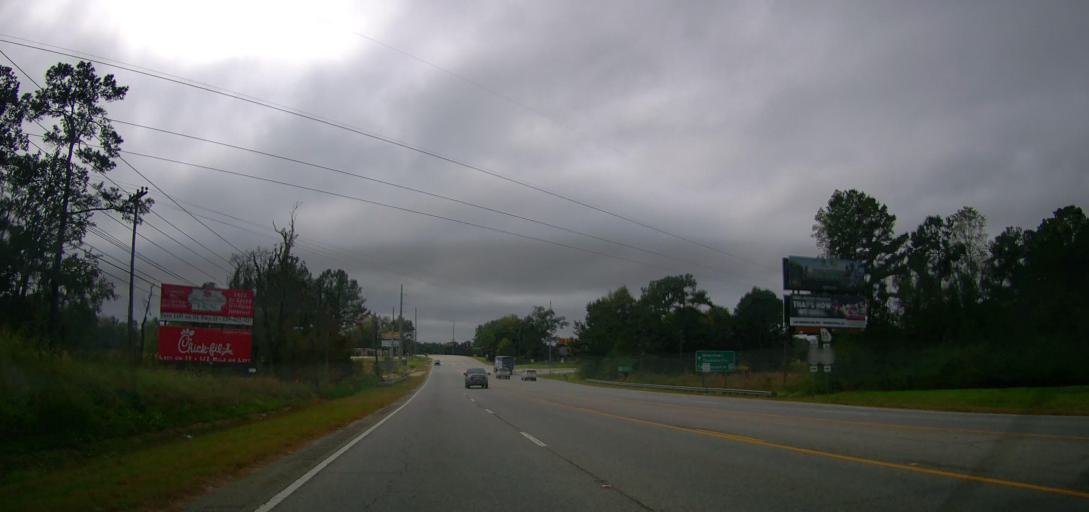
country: US
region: Georgia
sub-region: Thomas County
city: Thomasville
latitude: 30.8748
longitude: -83.9368
